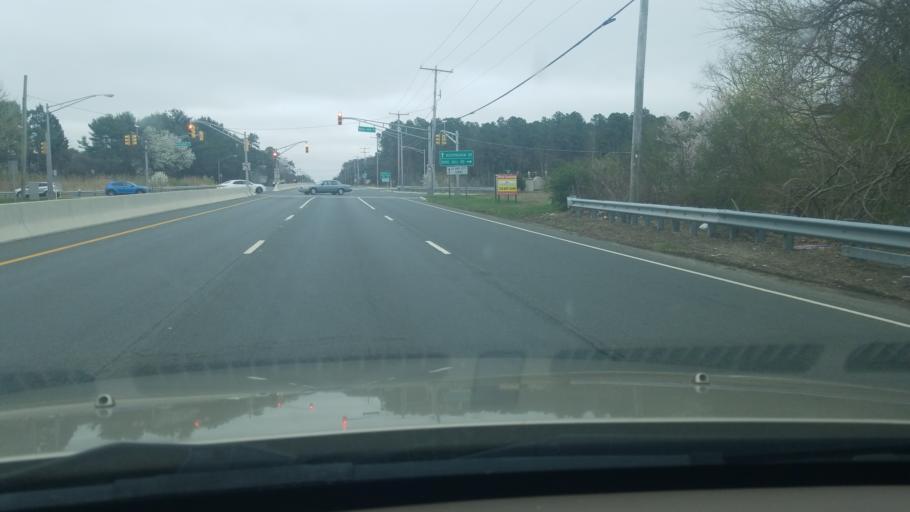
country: US
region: New Jersey
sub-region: Ocean County
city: Leisure Knoll
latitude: 40.0019
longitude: -74.2908
